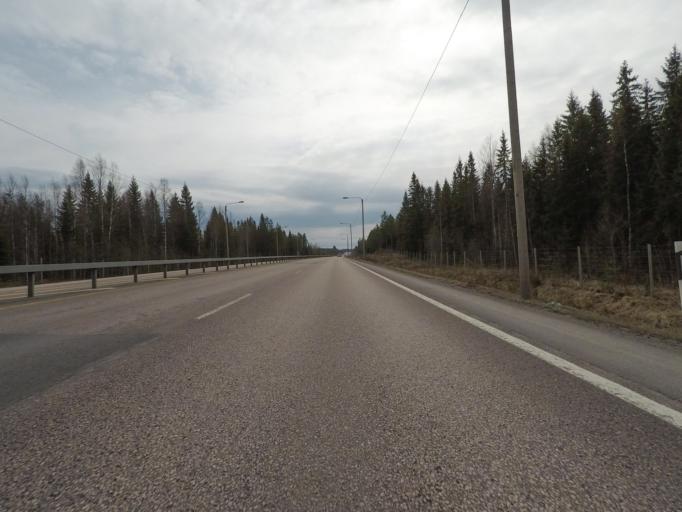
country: FI
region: Paijanne Tavastia
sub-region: Lahti
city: Hartola
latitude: 61.4789
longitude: 25.9805
